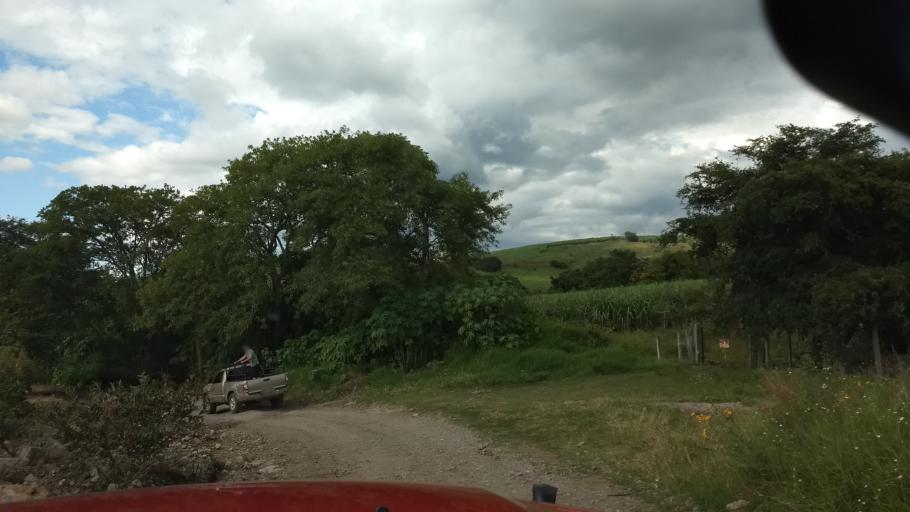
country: MX
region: Colima
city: Suchitlan
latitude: 19.4635
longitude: -103.7500
